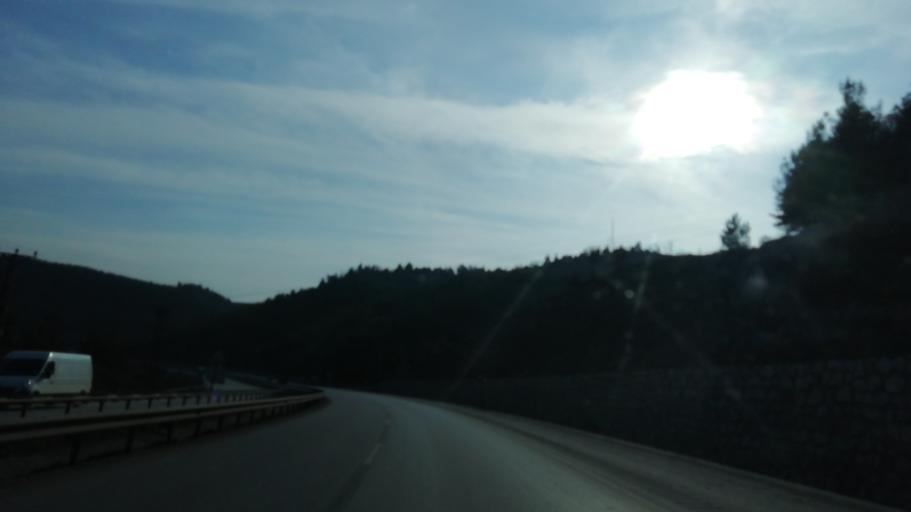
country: TR
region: Karabuk
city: Karabuk
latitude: 41.1623
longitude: 32.6399
